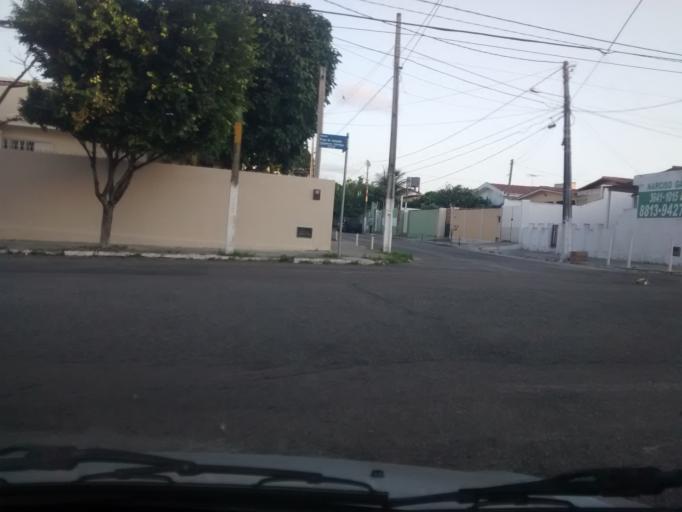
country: BR
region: Rio Grande do Norte
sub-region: Natal
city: Natal
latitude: -5.8708
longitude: -35.1884
